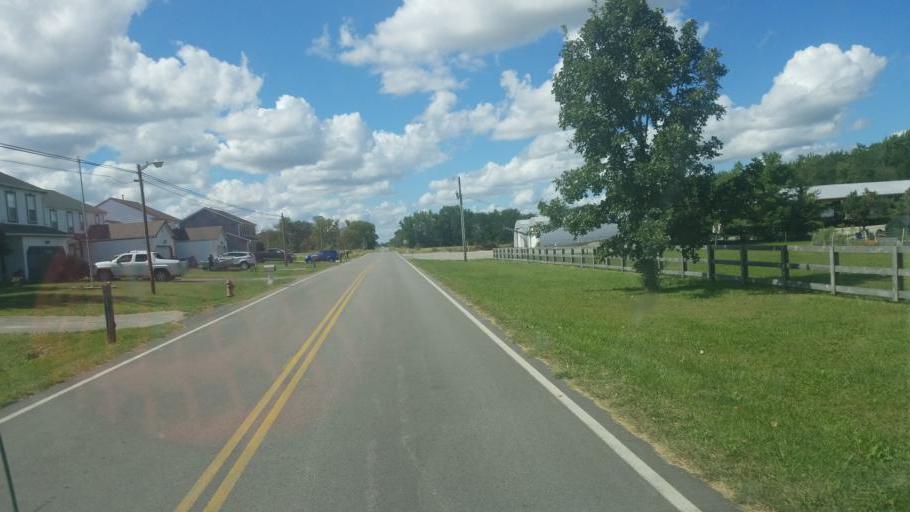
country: US
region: Ohio
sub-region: Union County
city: Marysville
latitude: 40.1818
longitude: -83.4475
